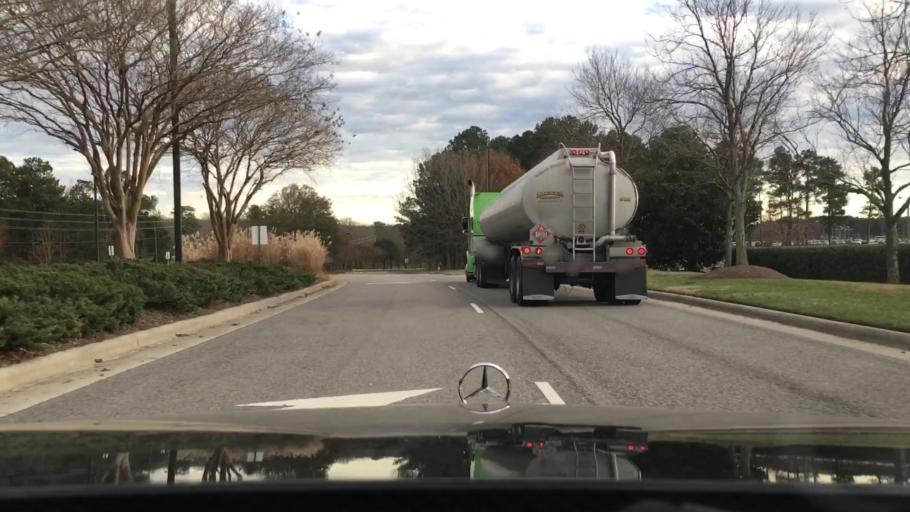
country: US
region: North Carolina
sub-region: Wake County
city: Morrisville
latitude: 35.8974
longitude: -78.7713
